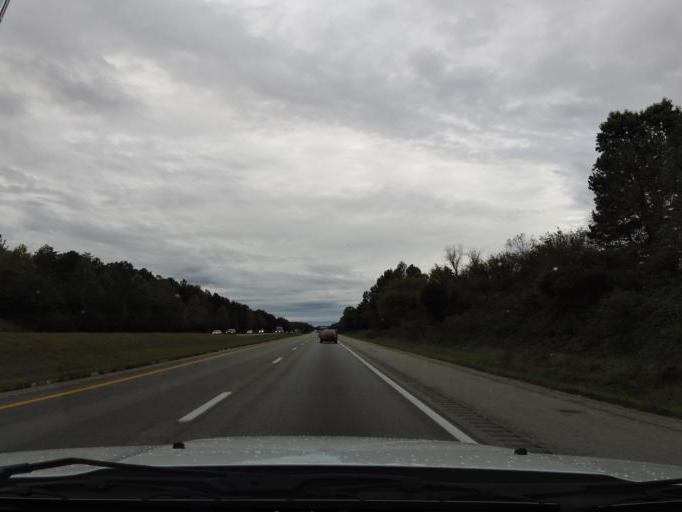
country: US
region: Kentucky
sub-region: Laurel County
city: London
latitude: 37.1892
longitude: -84.1436
